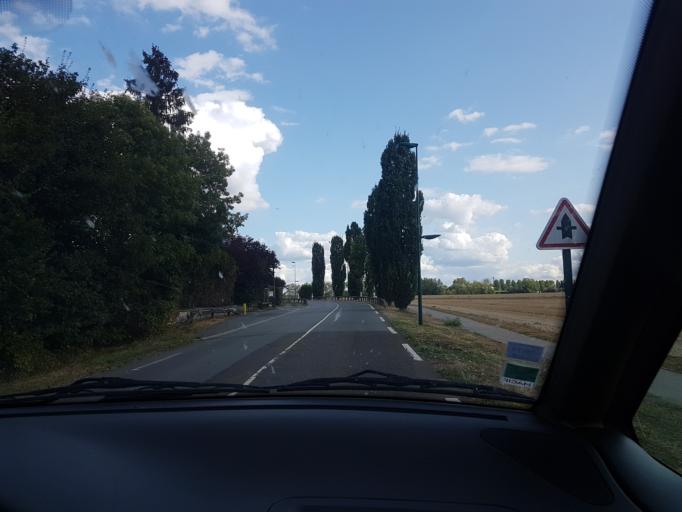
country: FR
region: Ile-de-France
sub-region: Departement des Yvelines
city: Plaisir
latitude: 48.8079
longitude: 1.9455
